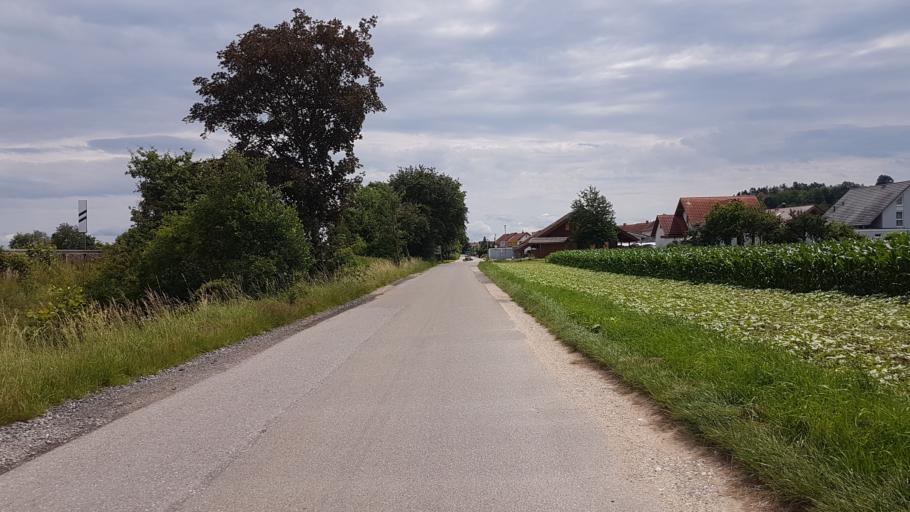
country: DE
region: Baden-Wuerttemberg
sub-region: Tuebingen Region
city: Ennetach
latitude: 48.0570
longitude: 9.3092
